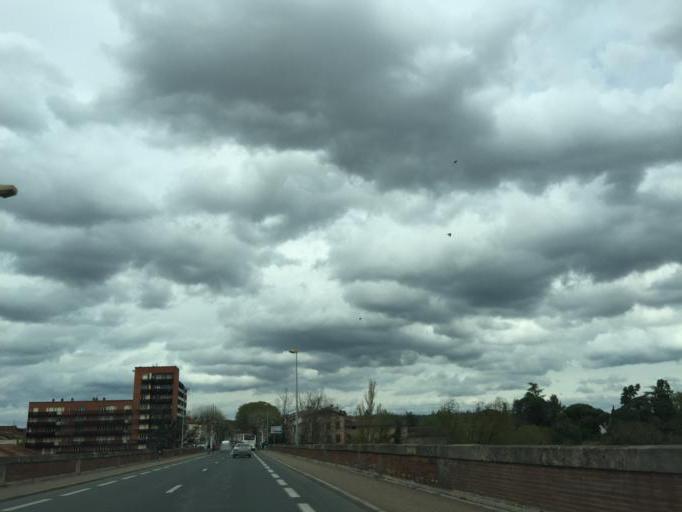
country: FR
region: Midi-Pyrenees
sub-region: Departement du Tarn
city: Albi
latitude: 43.9317
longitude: 2.1471
